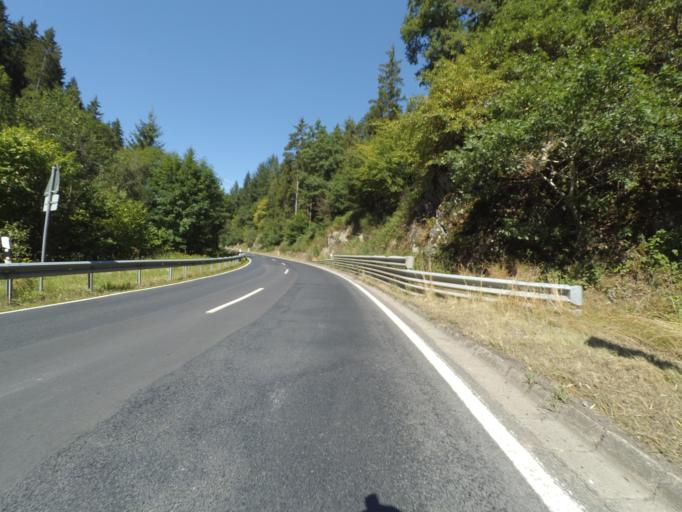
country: DE
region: Rheinland-Pfalz
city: Mullenbach
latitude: 50.2028
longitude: 7.0637
